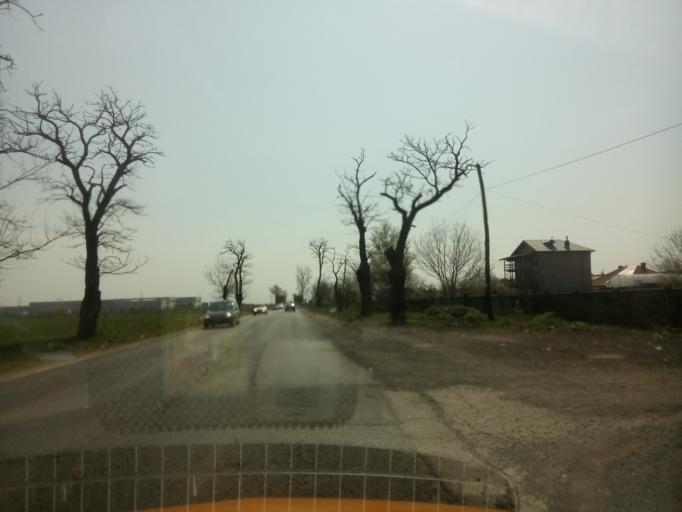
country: RO
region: Ilfov
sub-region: Comuna Berceni
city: Berceni
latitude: 44.3560
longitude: 26.2069
